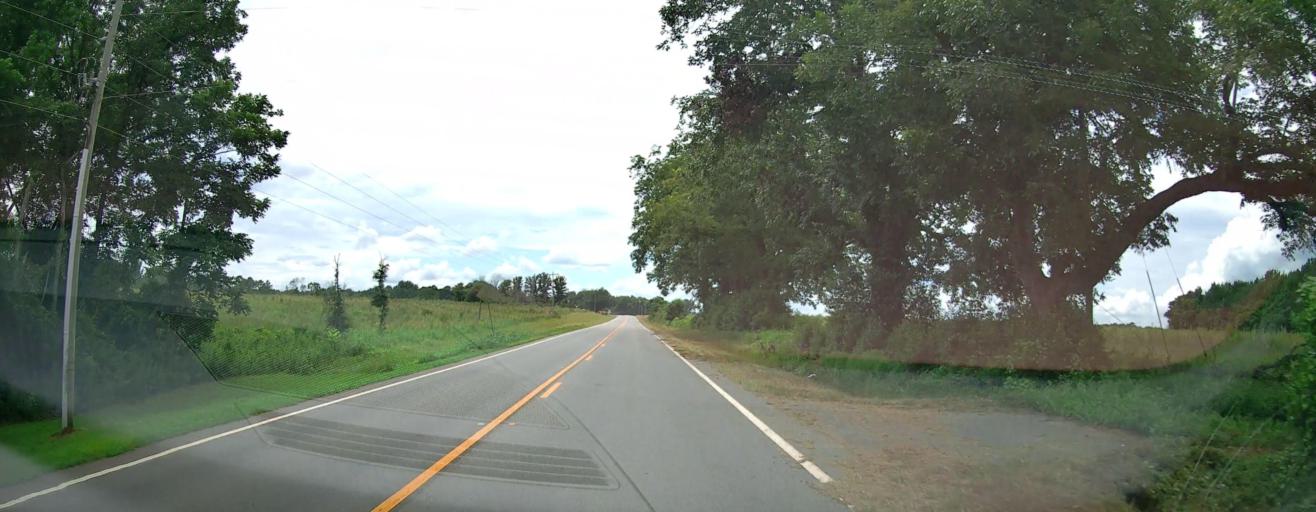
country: US
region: Georgia
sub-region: Macon County
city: Oglethorpe
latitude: 32.2839
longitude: -84.1642
